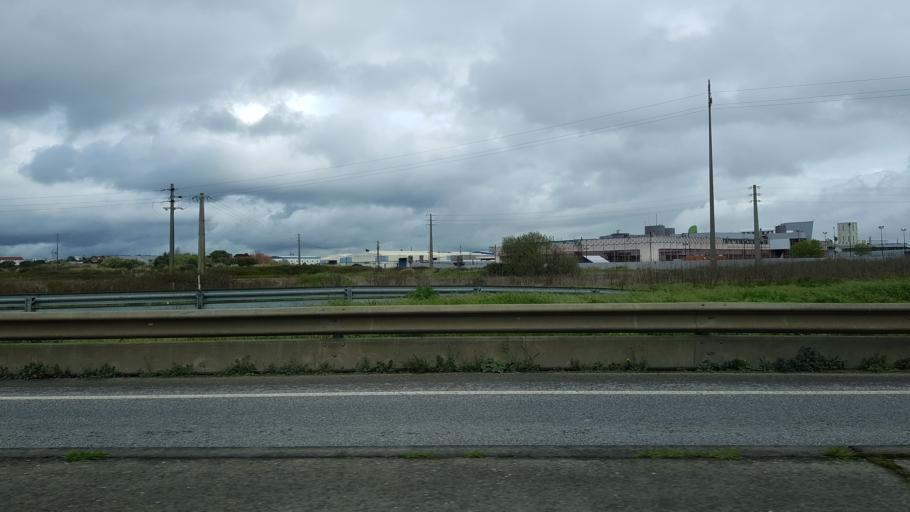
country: PT
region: Lisbon
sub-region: Alenquer
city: Carregado
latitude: 39.0348
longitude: -8.9818
